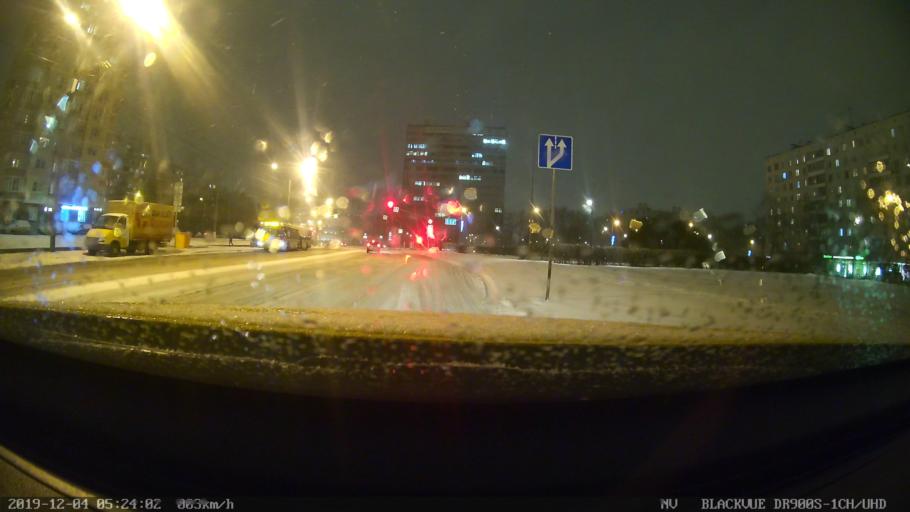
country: RU
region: Moscow
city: Khimki
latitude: 55.8546
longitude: 37.4380
